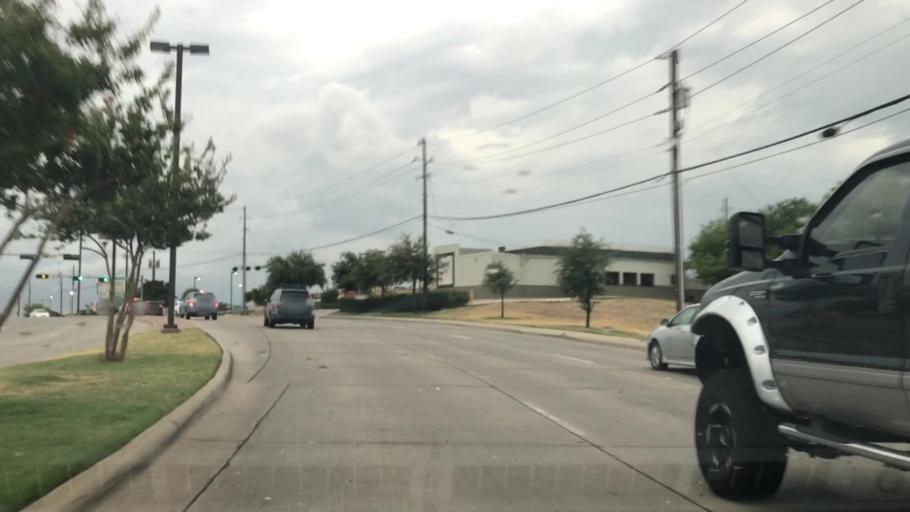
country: US
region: Texas
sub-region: Dallas County
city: Carrollton
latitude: 33.0013
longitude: -96.8865
